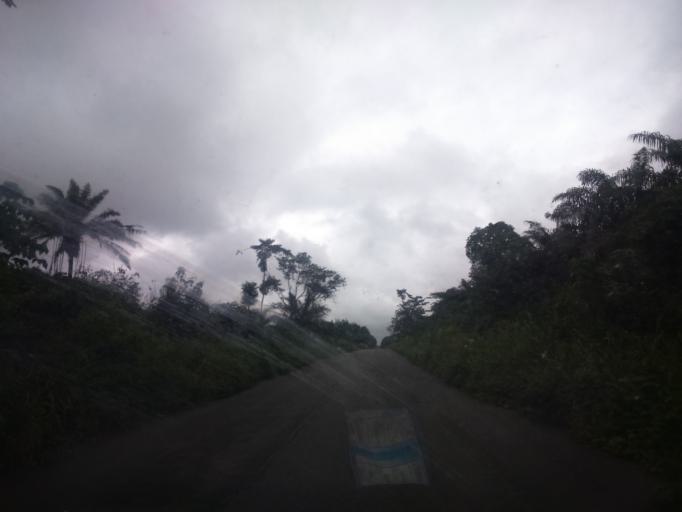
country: CI
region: Sud-Comoe
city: Bonoua
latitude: 5.2795
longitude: -3.4918
